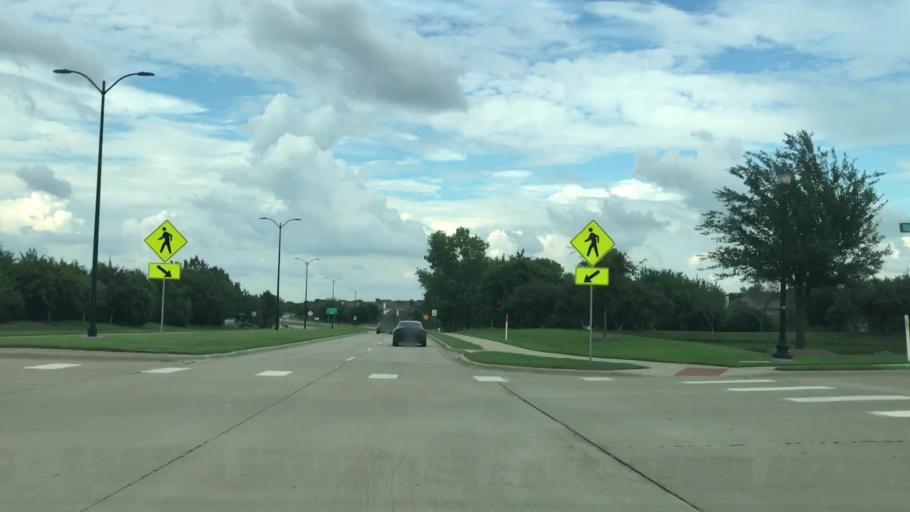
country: US
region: Texas
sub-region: Collin County
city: Frisco
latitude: 33.1793
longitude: -96.7845
